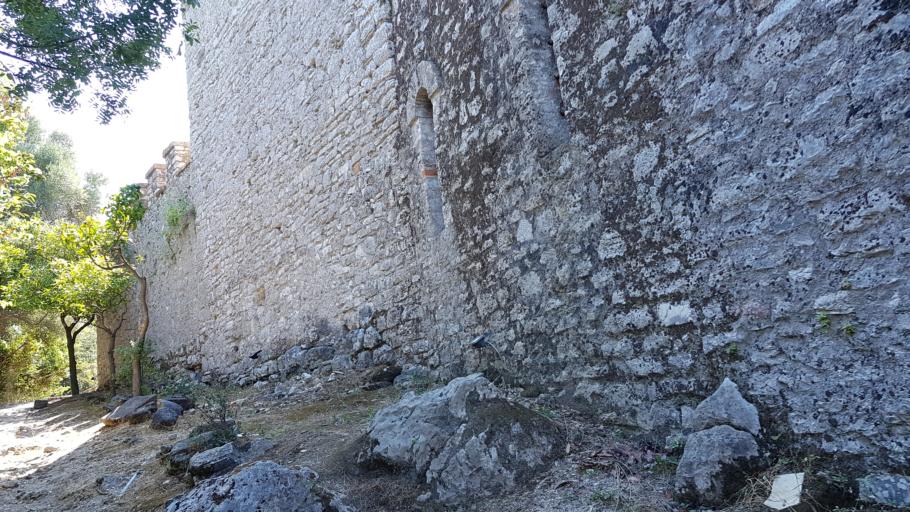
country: AL
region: Vlore
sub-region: Rrethi i Sarandes
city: Xarre
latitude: 39.7464
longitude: 20.0199
